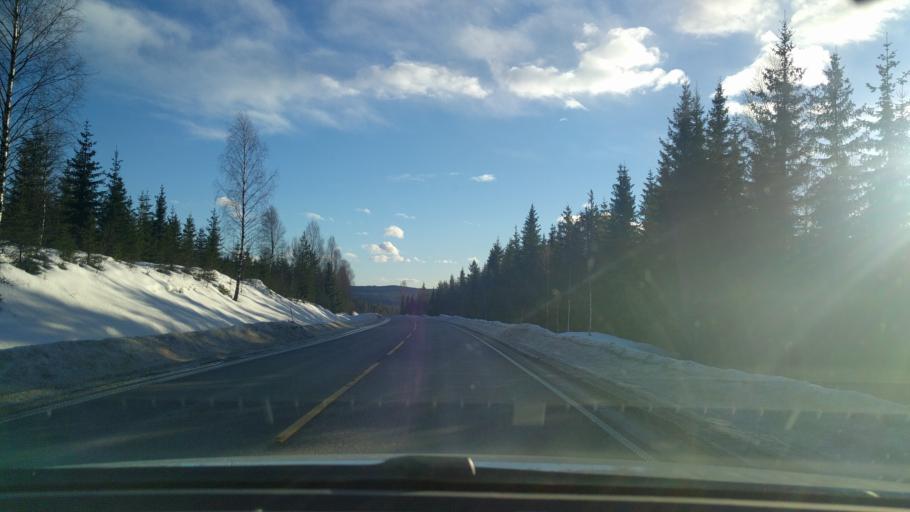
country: NO
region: Hedmark
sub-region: Trysil
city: Innbygda
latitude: 61.0992
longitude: 12.0046
